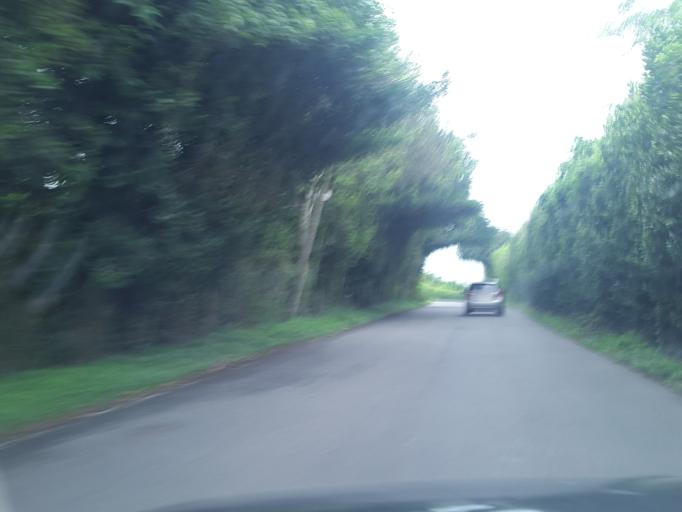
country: CO
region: Quindio
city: La Tebaida
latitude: 4.4865
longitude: -75.8003
